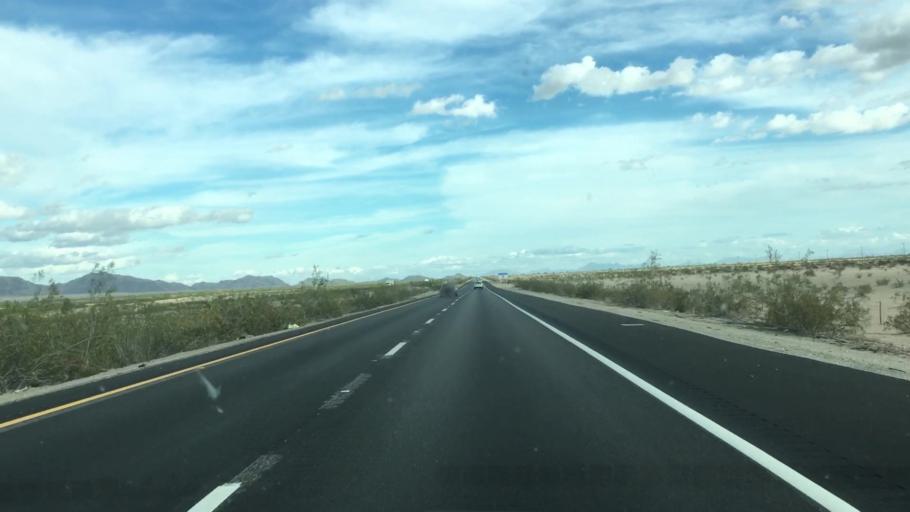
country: US
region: California
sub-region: Riverside County
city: Mesa Verde
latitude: 33.6083
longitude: -114.8813
